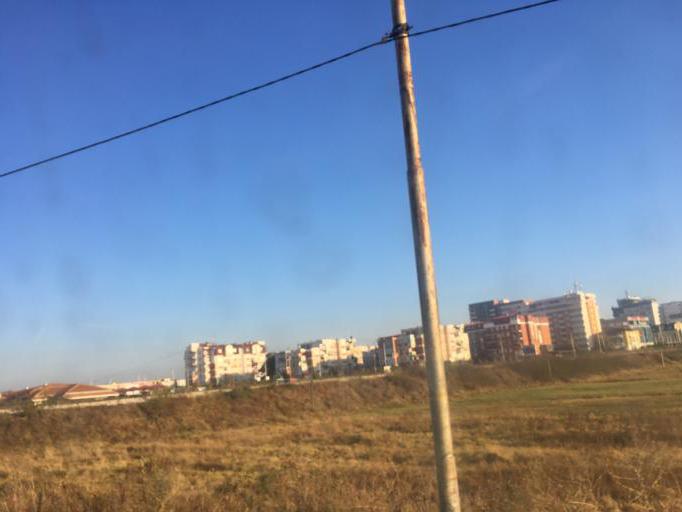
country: XK
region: Pristina
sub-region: Komuna e Drenasit
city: Glogovac
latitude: 42.6196
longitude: 20.8943
